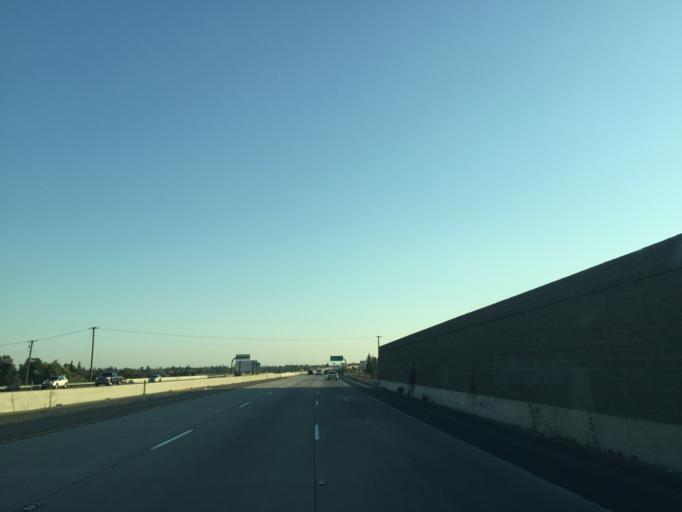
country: US
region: California
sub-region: Fresno County
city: Tarpey Village
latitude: 36.8029
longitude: -119.7388
